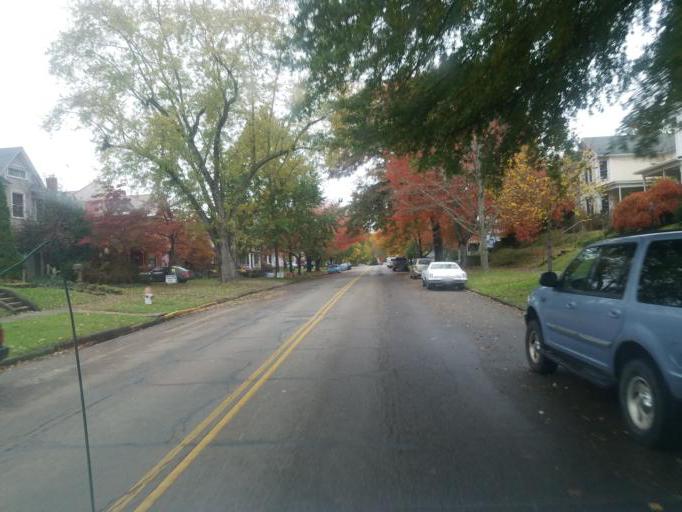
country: US
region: Ohio
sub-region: Washington County
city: Marietta
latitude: 39.4241
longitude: -81.4636
